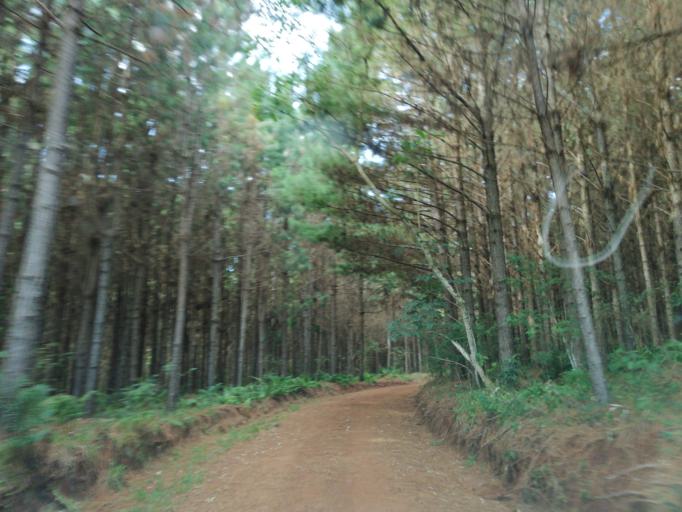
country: AR
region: Misiones
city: Dos de Mayo
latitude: -27.0162
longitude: -54.4199
